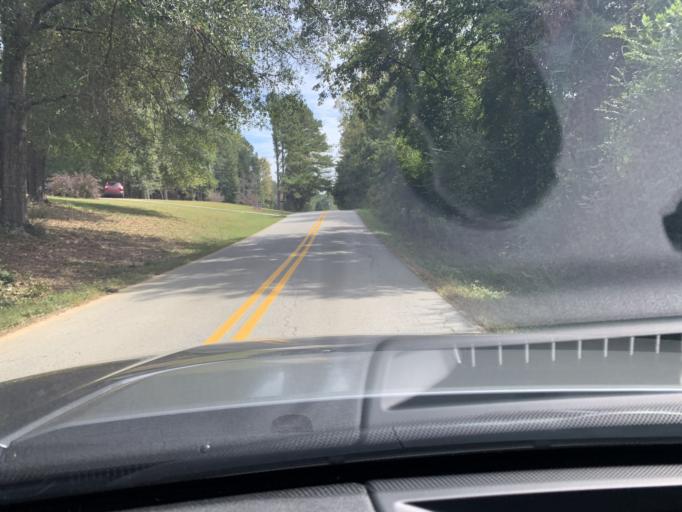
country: US
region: Georgia
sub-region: Polk County
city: Cedartown
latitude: 33.9743
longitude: -85.2816
